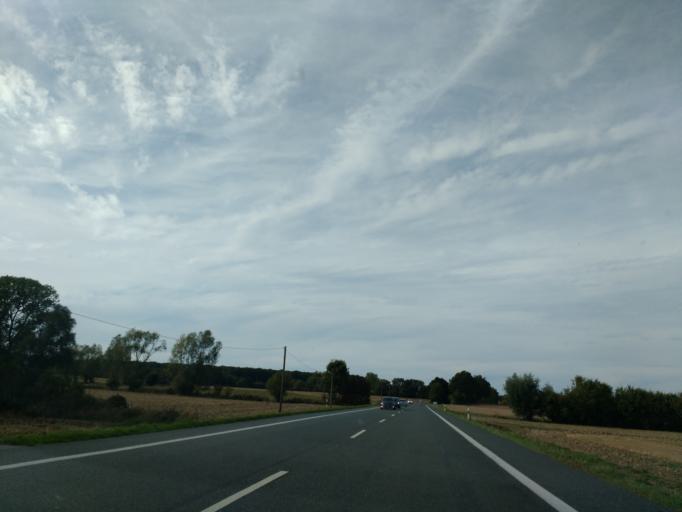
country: DE
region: North Rhine-Westphalia
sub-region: Regierungsbezirk Detmold
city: Nieheim
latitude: 51.8180
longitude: 9.0945
